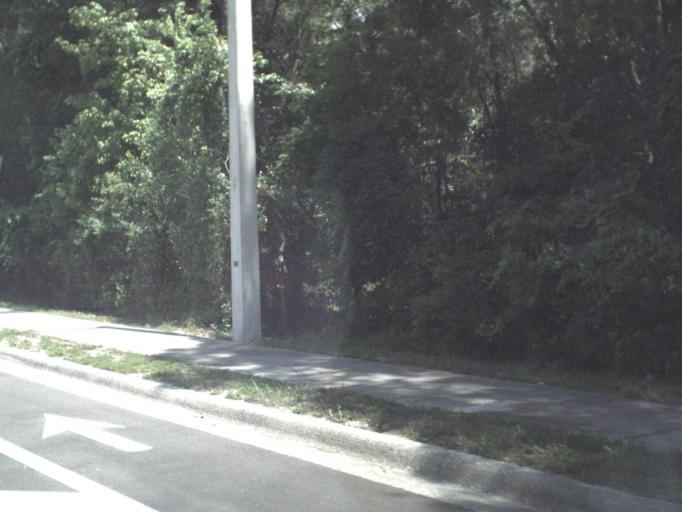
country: US
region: Florida
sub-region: Alachua County
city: Gainesville
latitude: 29.6425
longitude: -82.2882
